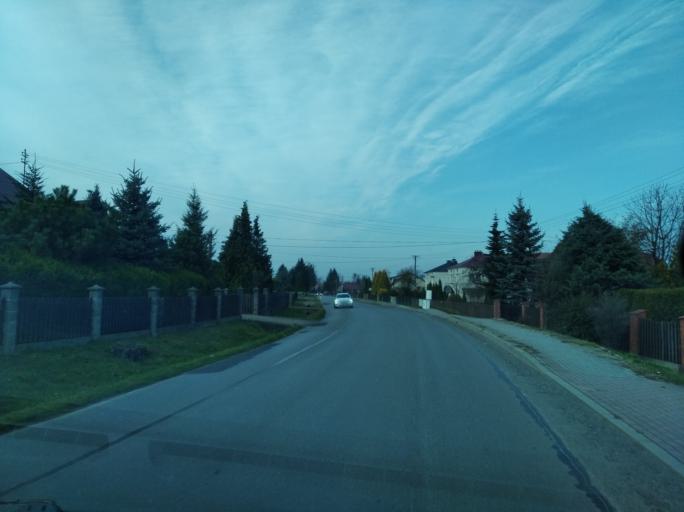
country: PL
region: Subcarpathian Voivodeship
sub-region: Powiat ropczycko-sedziszowski
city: Iwierzyce
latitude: 50.0520
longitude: 21.7458
